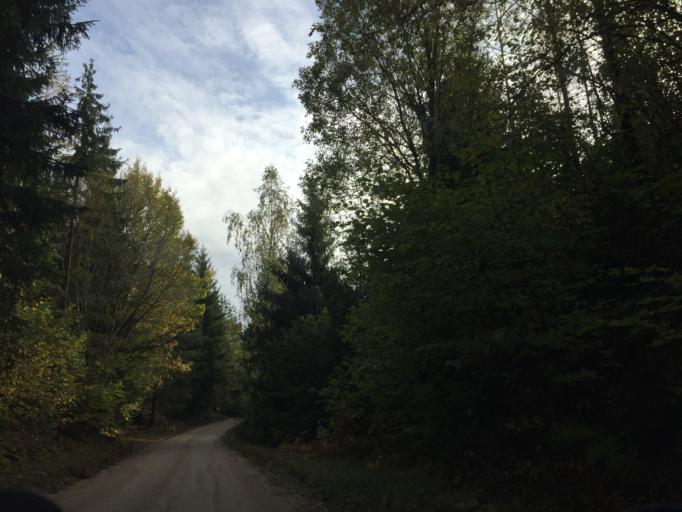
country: LV
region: Jaunpils
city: Jaunpils
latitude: 56.5855
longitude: 23.0122
